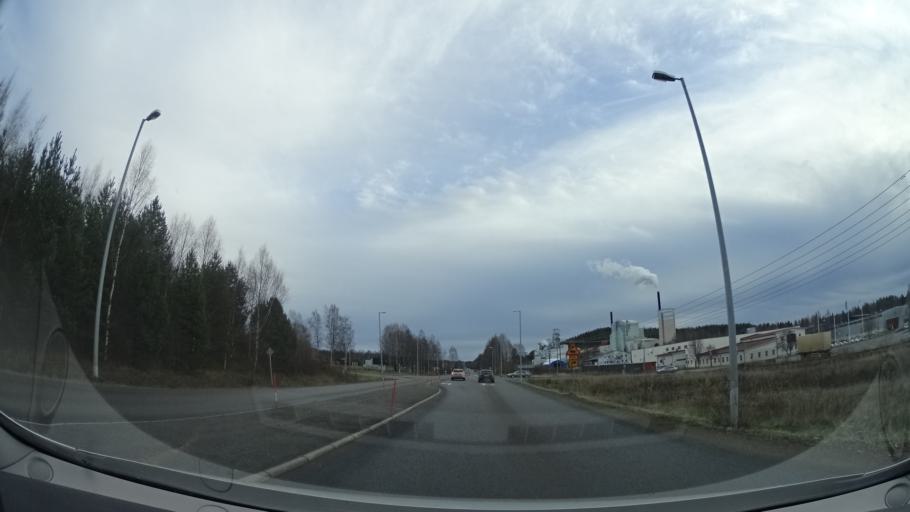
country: SE
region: Vaesterbotten
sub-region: Skelleftea Kommun
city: Soedra Bergsbyn
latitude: 64.7479
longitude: 21.0335
